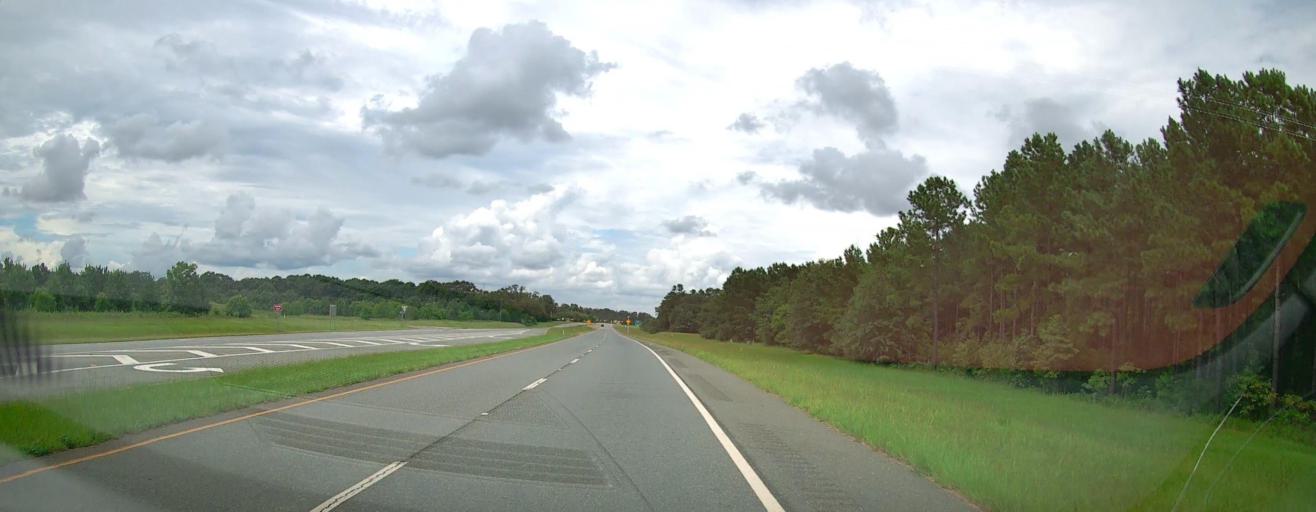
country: US
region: Georgia
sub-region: Schley County
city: Ellaville
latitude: 32.2346
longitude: -84.2939
